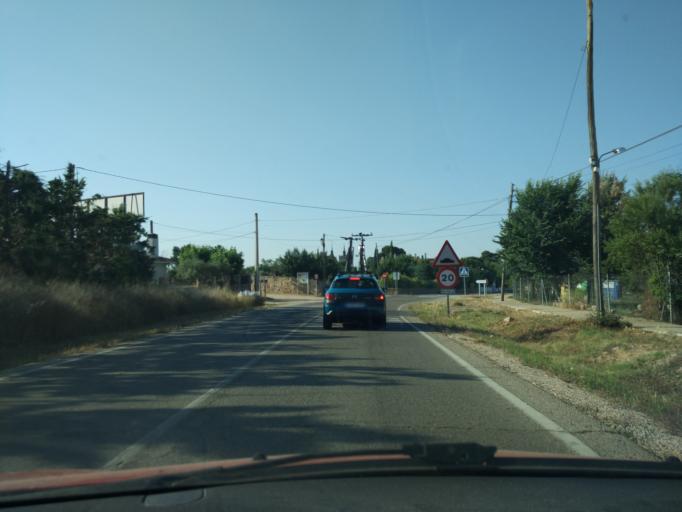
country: ES
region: Madrid
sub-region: Provincia de Madrid
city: Nuevo Baztan
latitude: 40.3698
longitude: -3.2445
